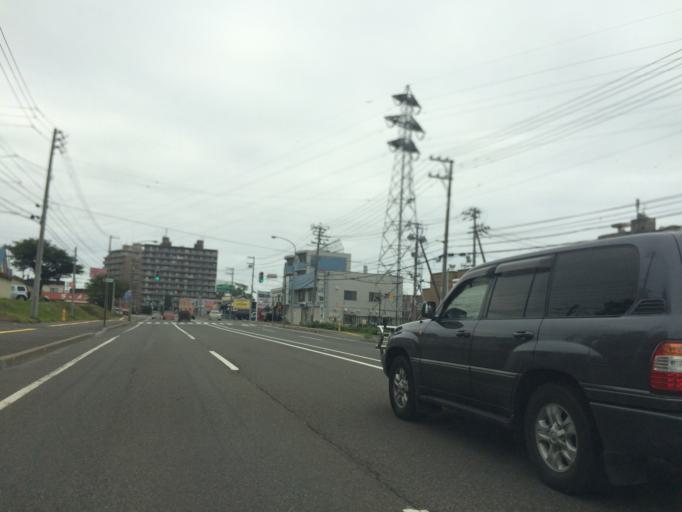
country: JP
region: Hokkaido
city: Sapporo
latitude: 43.1294
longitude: 141.2116
